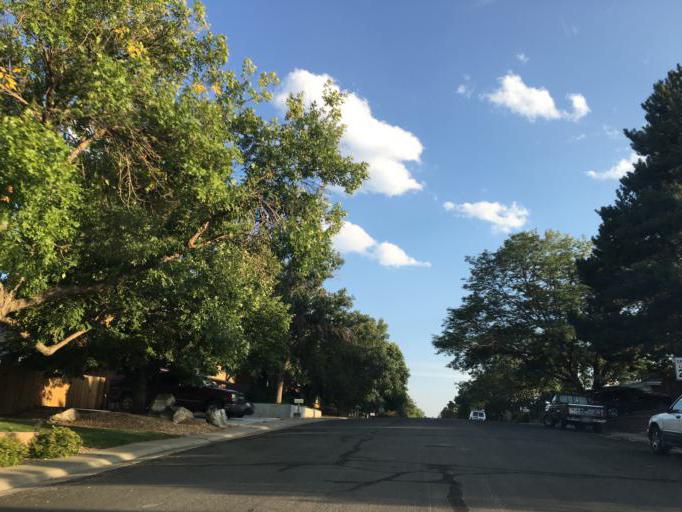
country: US
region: Colorado
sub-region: Jefferson County
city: Applewood
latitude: 39.7943
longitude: -105.1474
